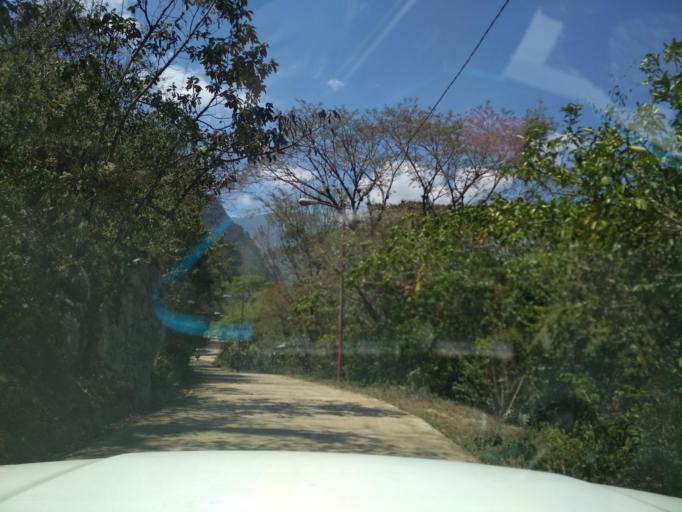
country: MX
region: Veracruz
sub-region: Tlilapan
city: Tonalixco
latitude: 18.7825
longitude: -97.0822
